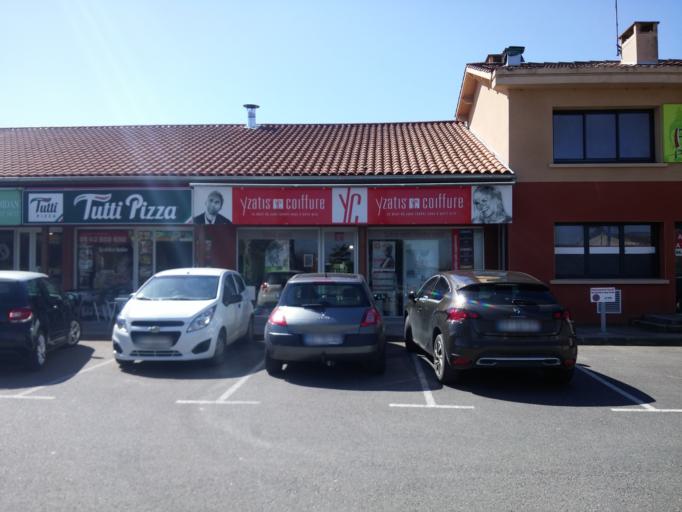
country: FR
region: Midi-Pyrenees
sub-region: Departement du Gers
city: Pujaudran
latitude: 43.6131
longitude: 1.0875
